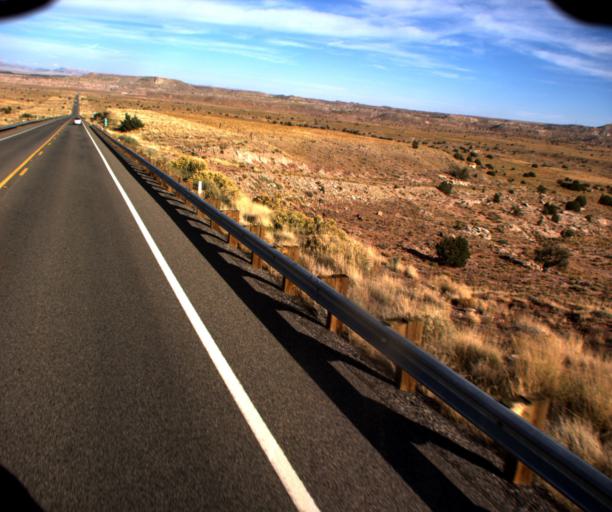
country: US
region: New Mexico
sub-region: San Juan County
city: Shiprock
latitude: 36.9288
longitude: -109.1605
